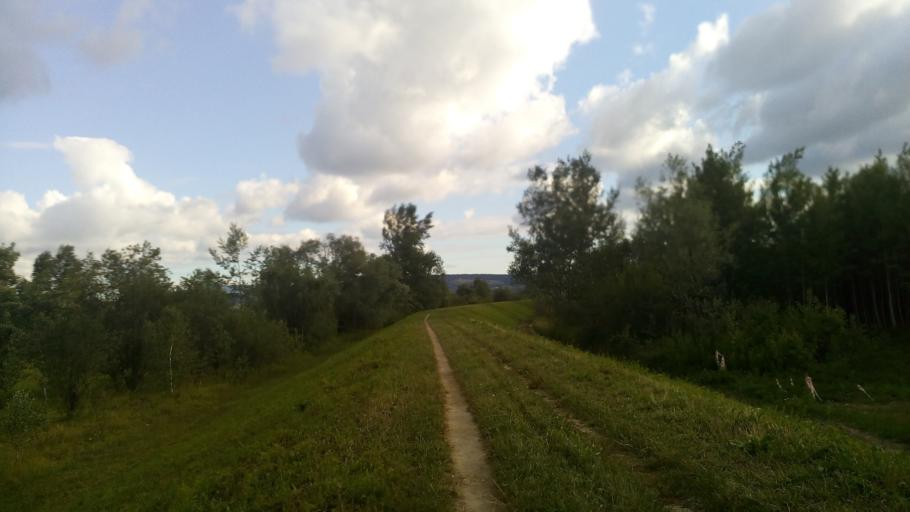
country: PL
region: Lesser Poland Voivodeship
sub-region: Powiat nowosadecki
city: Stary Sacz
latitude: 49.5888
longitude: 20.6540
